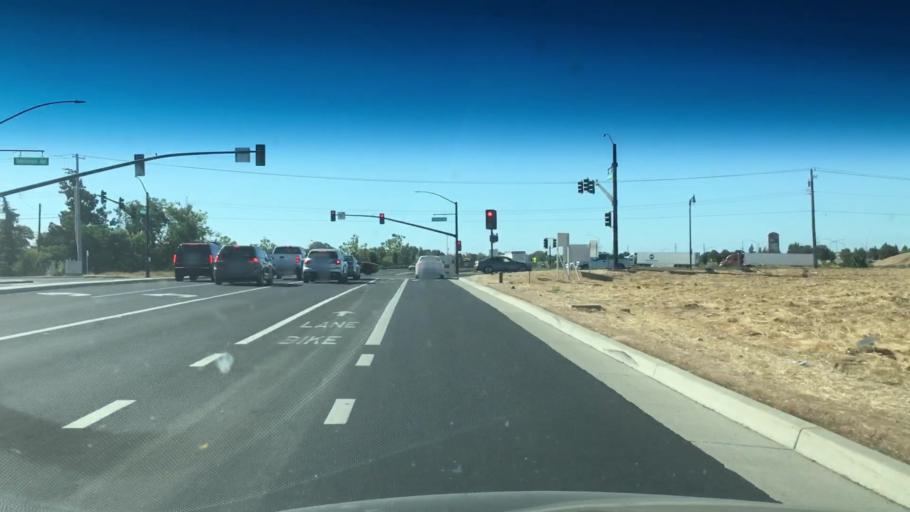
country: US
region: California
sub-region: Sacramento County
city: Laguna
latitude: 38.4388
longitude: -121.3974
